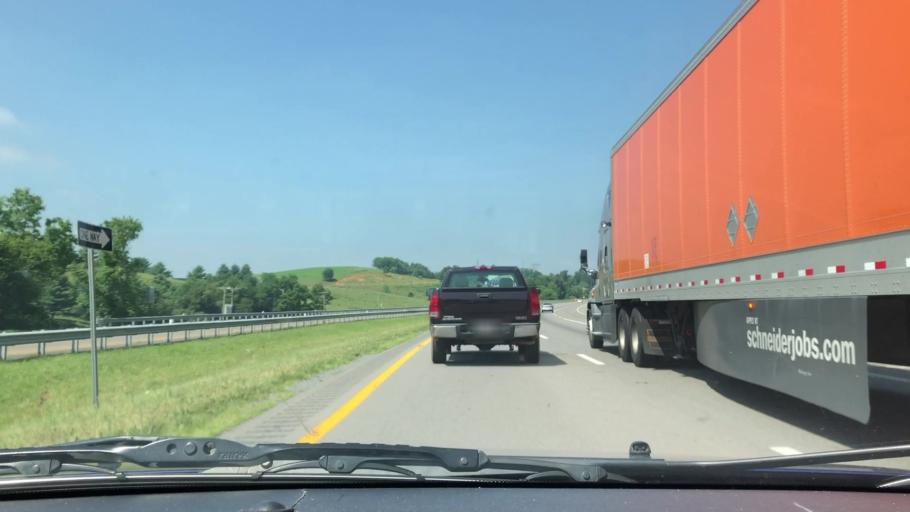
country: US
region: Virginia
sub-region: Washington County
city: Glade Spring
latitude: 36.7822
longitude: -81.7371
